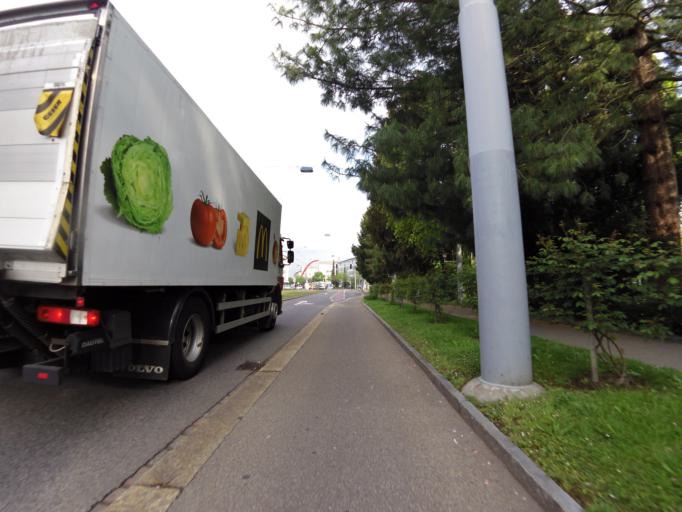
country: CH
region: Zurich
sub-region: Bezirk Zuerich
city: Zuerich (Kreis 9) / Altstetten
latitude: 47.3864
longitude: 8.4918
